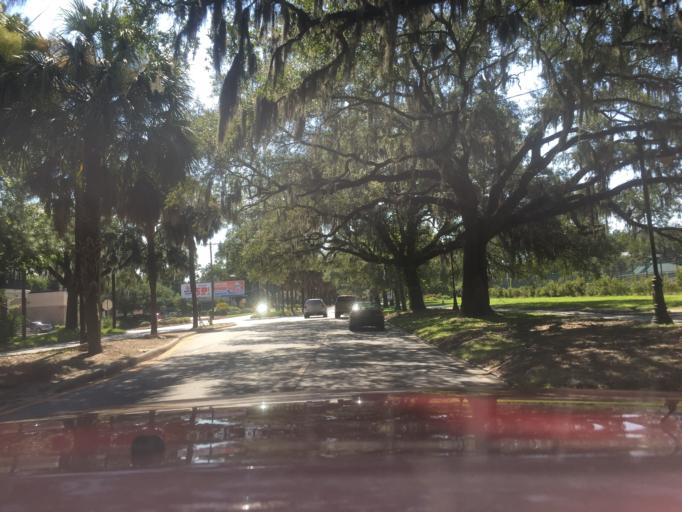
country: US
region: Georgia
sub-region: Chatham County
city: Thunderbolt
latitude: 32.0469
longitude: -81.0806
